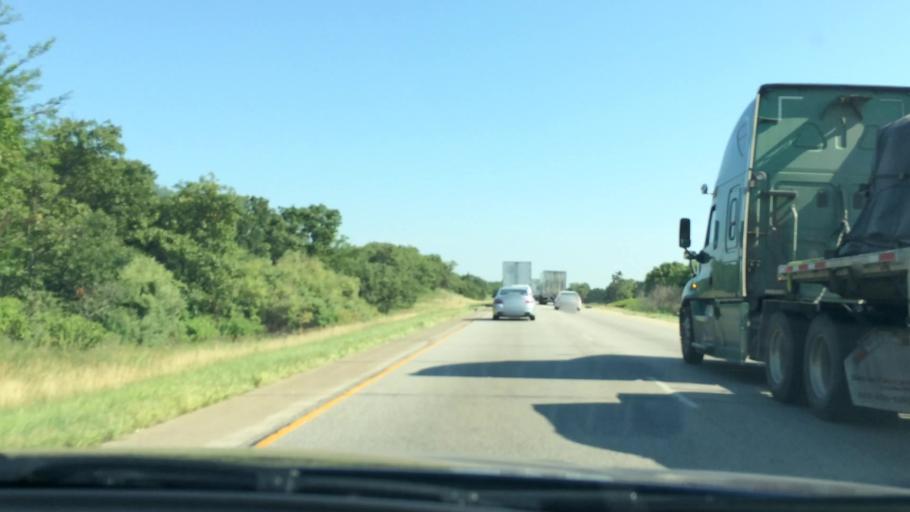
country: US
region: Indiana
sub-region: Newton County
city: Roselawn
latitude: 41.0306
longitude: -87.2702
